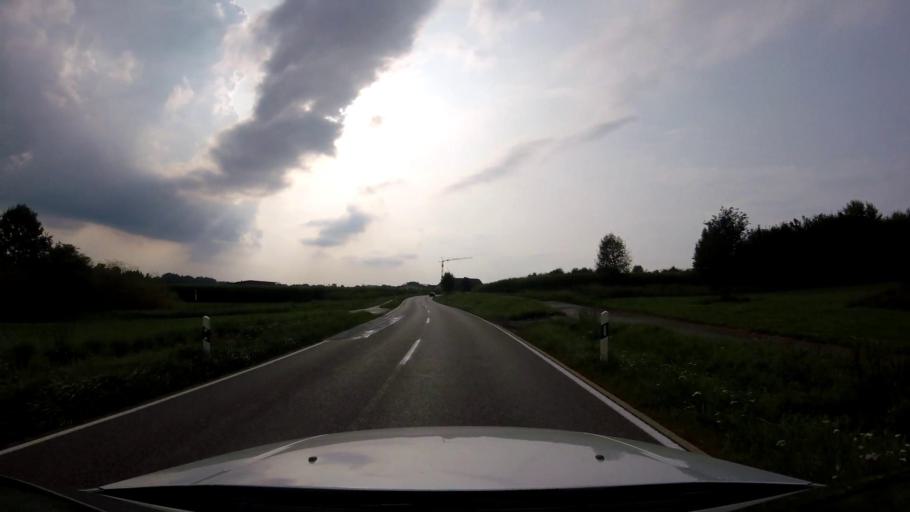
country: DE
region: Baden-Wuerttemberg
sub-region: Regierungsbezirk Stuttgart
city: Mutlangen
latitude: 48.8368
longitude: 9.7855
